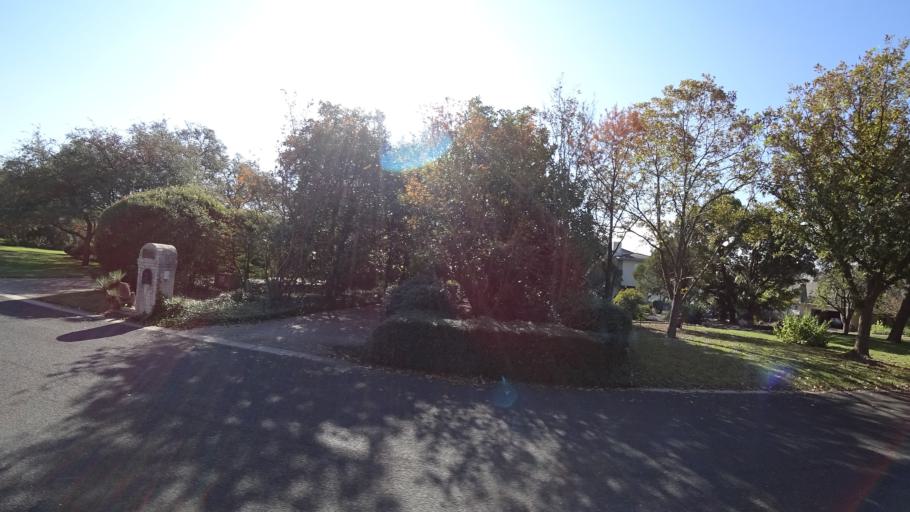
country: US
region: Texas
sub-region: Williamson County
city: Anderson Mill
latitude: 30.3773
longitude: -97.8215
